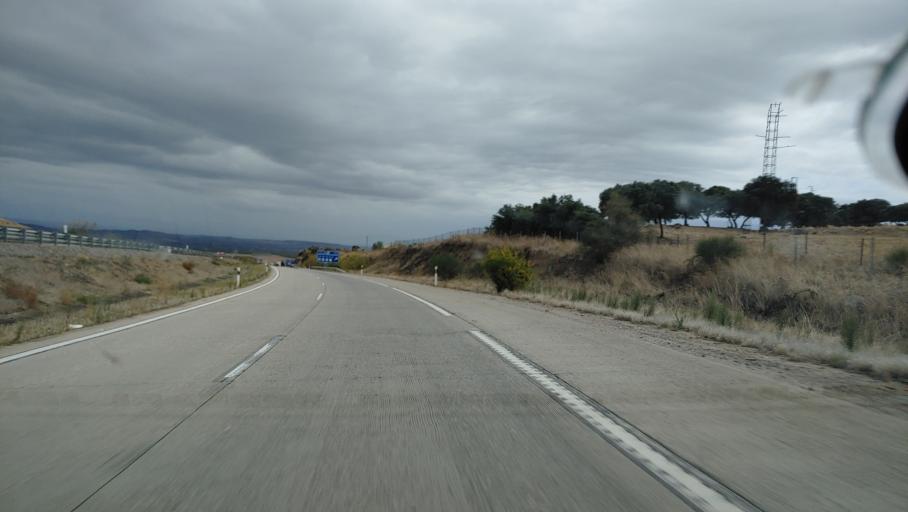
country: ES
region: Andalusia
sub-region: Provincia de Jaen
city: La Carolina
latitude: 38.3084
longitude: -3.5775
